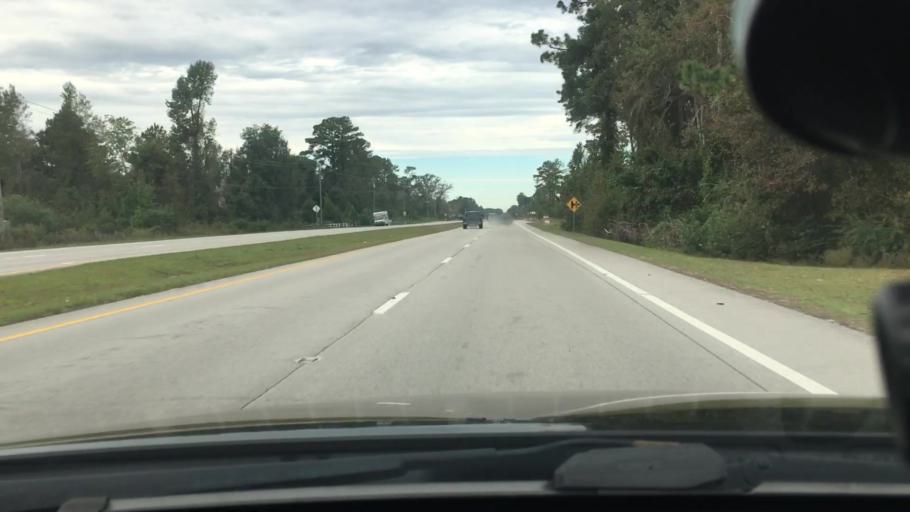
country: US
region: North Carolina
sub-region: Craven County
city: New Bern
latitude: 35.1367
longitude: -77.0274
